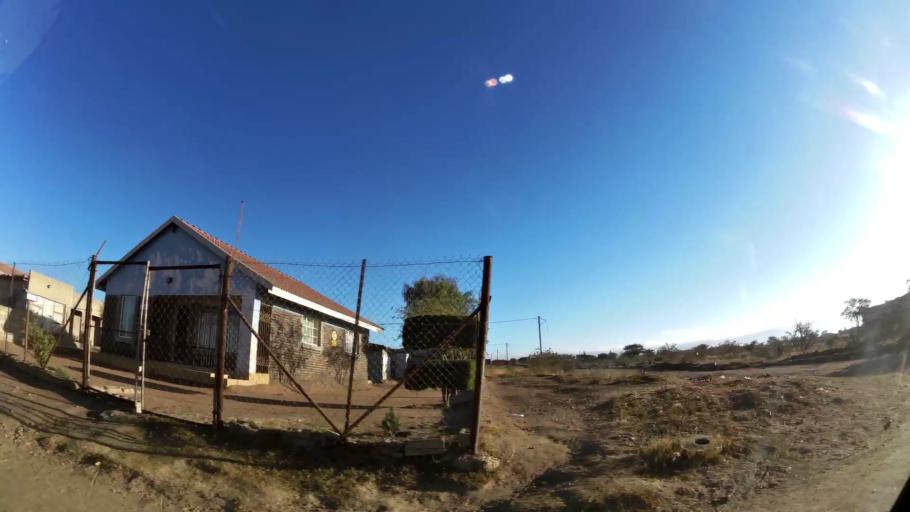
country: ZA
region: Limpopo
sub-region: Capricorn District Municipality
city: Polokwane
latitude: -23.8420
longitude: 29.3502
